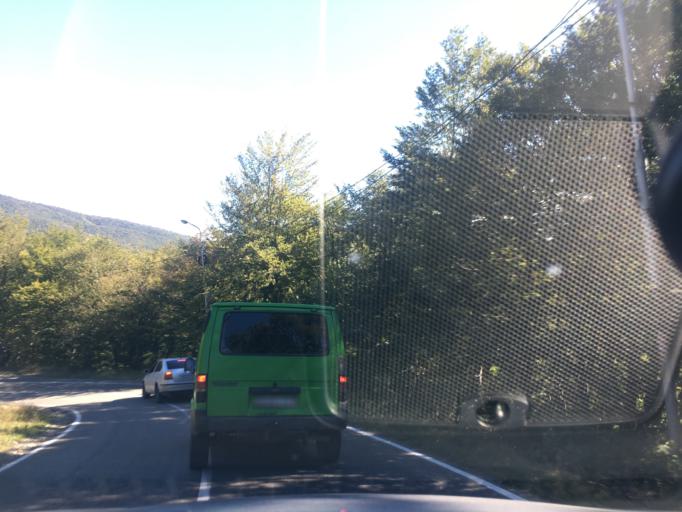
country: GE
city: Didi Lilo
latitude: 41.8756
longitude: 44.9117
